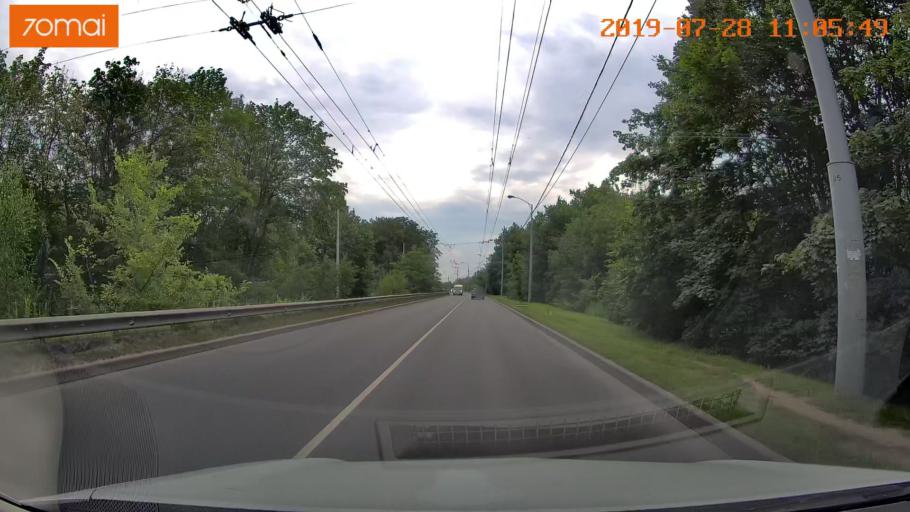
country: RU
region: Kaliningrad
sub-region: Gorod Kaliningrad
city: Kaliningrad
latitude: 54.7164
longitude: 20.3993
